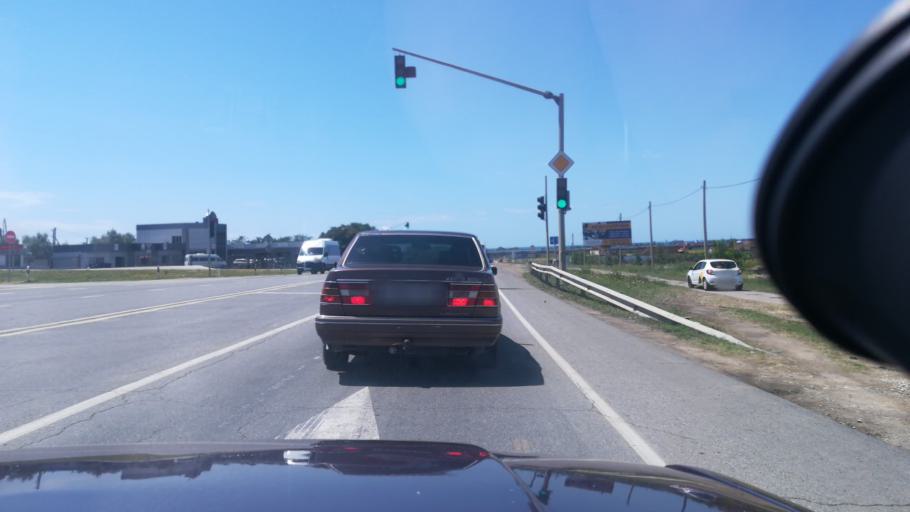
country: RU
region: Krasnodarskiy
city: Tsibanobalka
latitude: 44.9656
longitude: 37.3161
